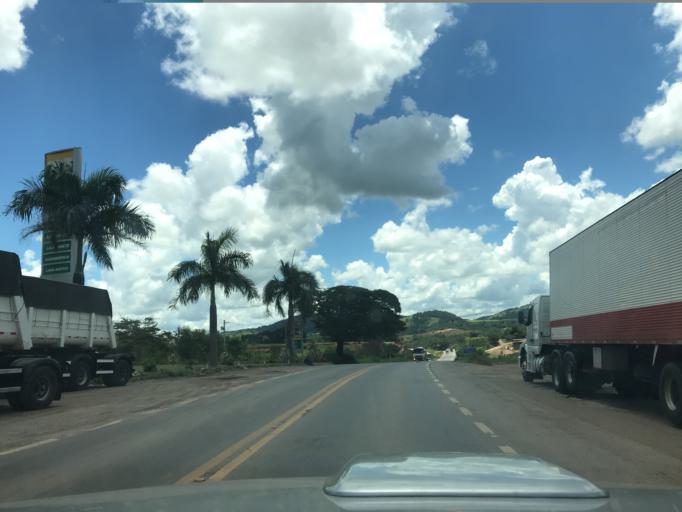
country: BR
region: Minas Gerais
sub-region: Perdoes
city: Perdoes
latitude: -21.1055
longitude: -45.0935
